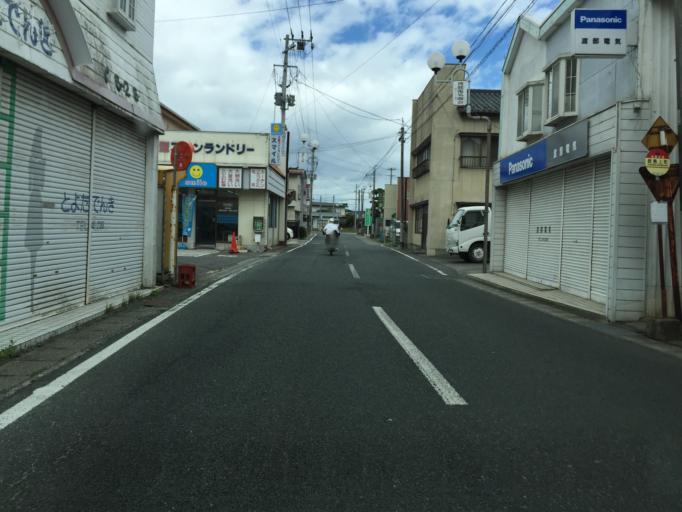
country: JP
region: Fukushima
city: Namie
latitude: 37.7053
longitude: 140.9659
